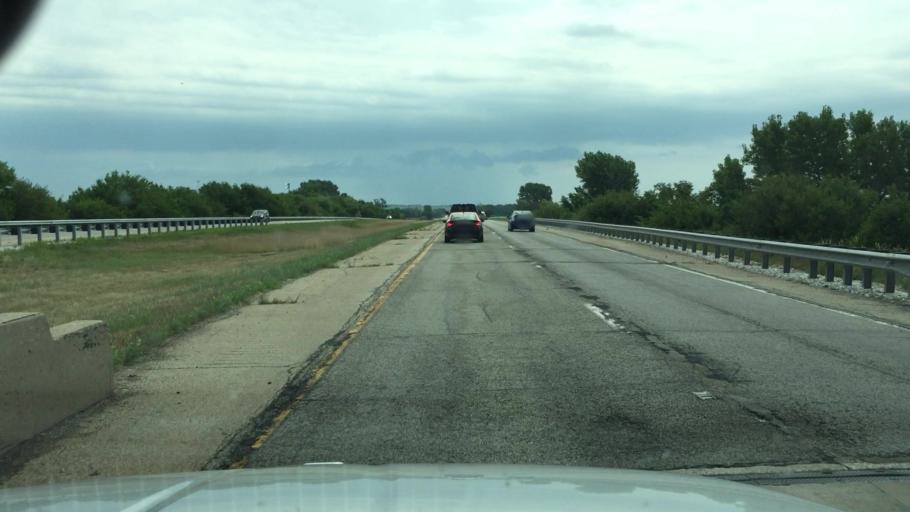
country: US
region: Illinois
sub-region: Peoria County
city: Elmwood
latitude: 40.8348
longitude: -89.8893
